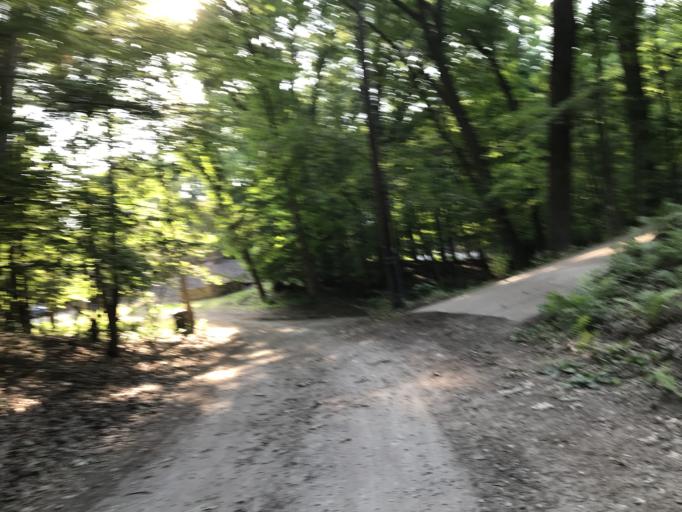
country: US
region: Michigan
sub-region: Oakland County
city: Farmington
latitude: 42.4725
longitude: -83.3853
